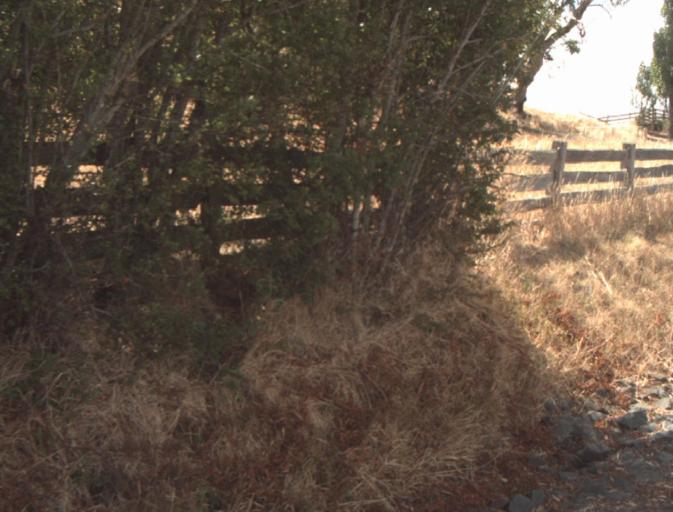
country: AU
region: Tasmania
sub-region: Launceston
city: Newstead
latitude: -41.4768
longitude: 147.1890
